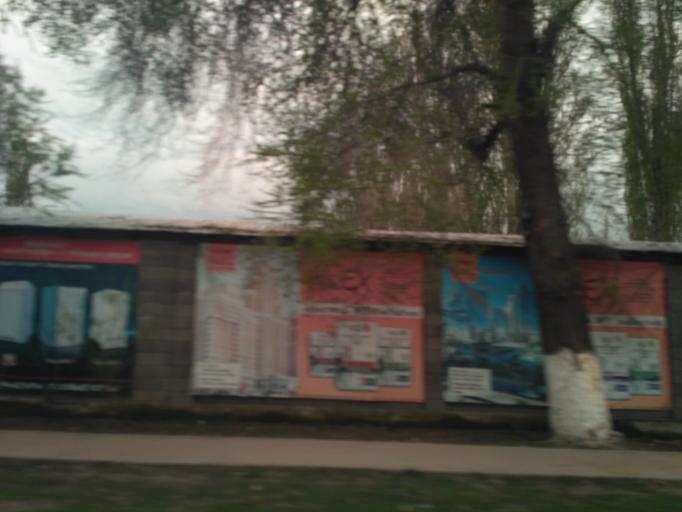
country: KZ
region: Almaty Oblysy
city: Burunday
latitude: 43.2110
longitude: 76.3199
